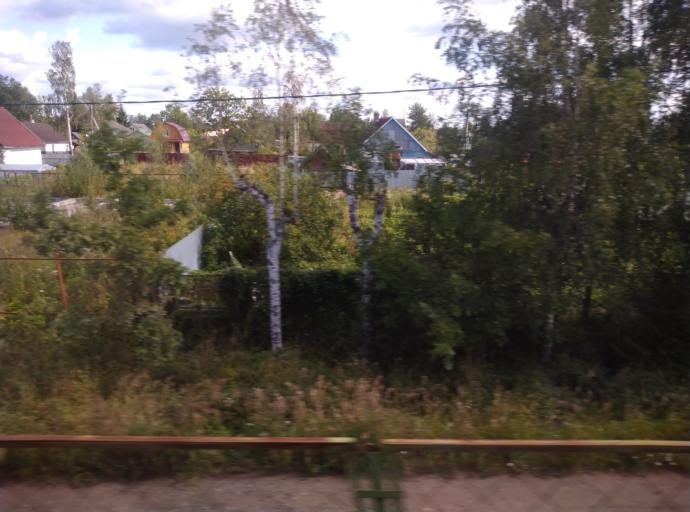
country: RU
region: Leningrad
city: Ul'yanovka
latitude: 59.6434
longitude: 30.7468
